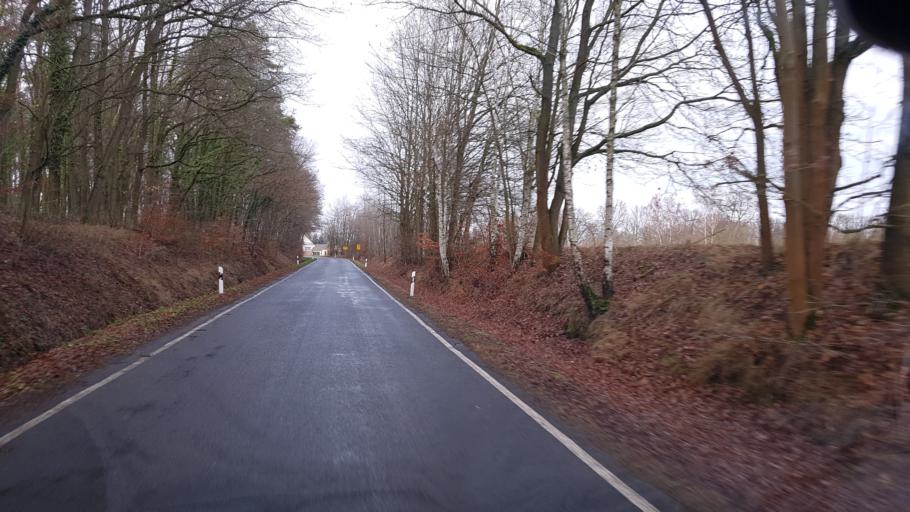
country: DE
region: Brandenburg
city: Altdobern
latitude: 51.6610
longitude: 13.9964
